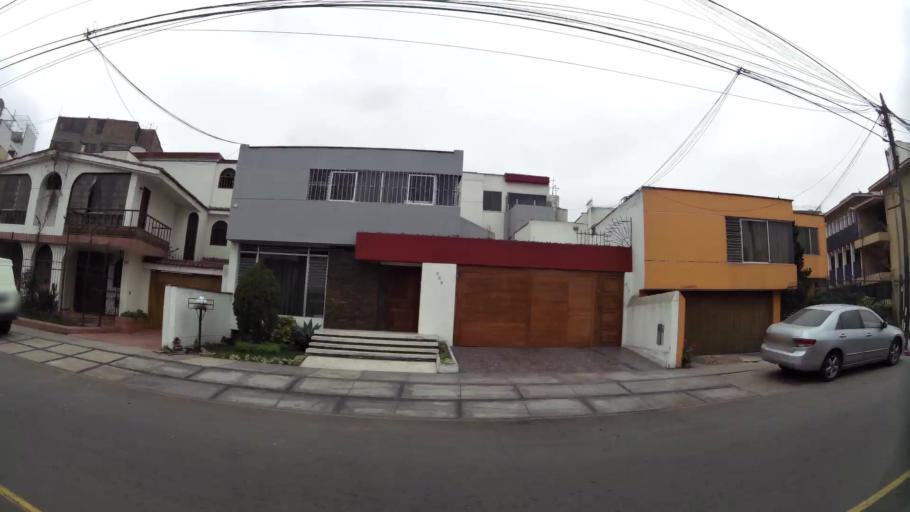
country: PE
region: Lima
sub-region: Lima
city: San Luis
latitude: -12.0908
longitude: -77.0151
